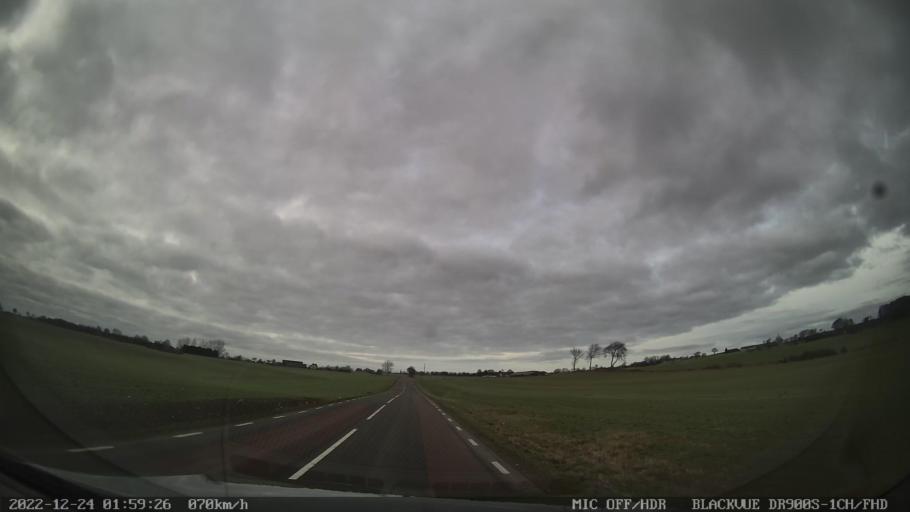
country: SE
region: Skane
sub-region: Tomelilla Kommun
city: Tomelilla
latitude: 55.6081
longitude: 14.0157
